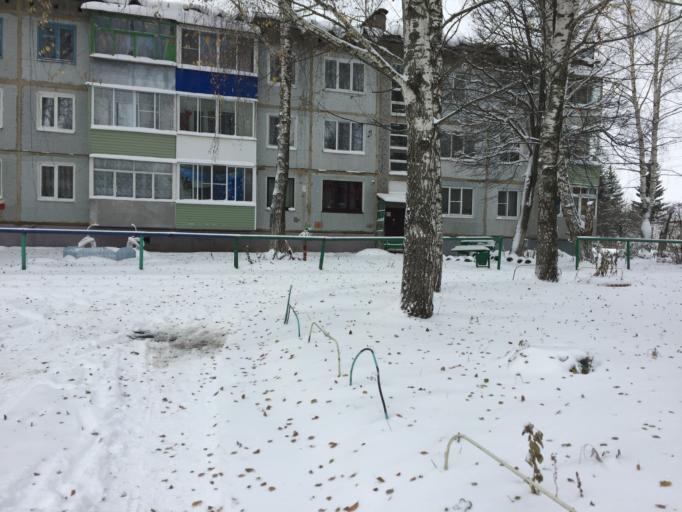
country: RU
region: Tula
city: Shchekino
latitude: 53.8516
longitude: 37.4810
